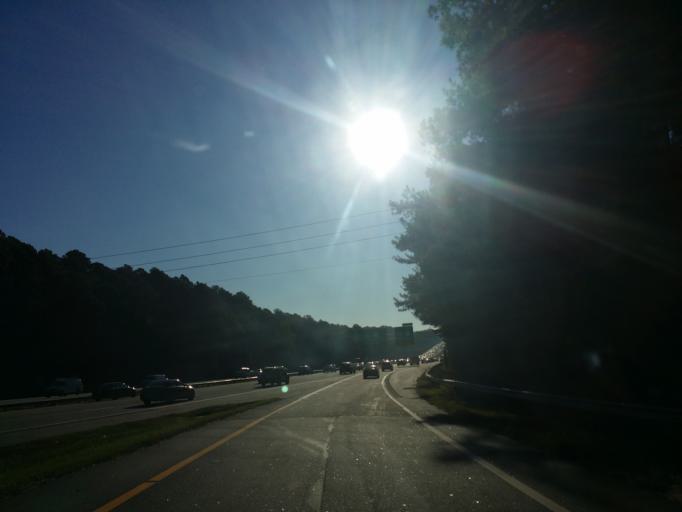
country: US
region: North Carolina
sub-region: Wake County
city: Cary
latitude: 35.8301
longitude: -78.7616
